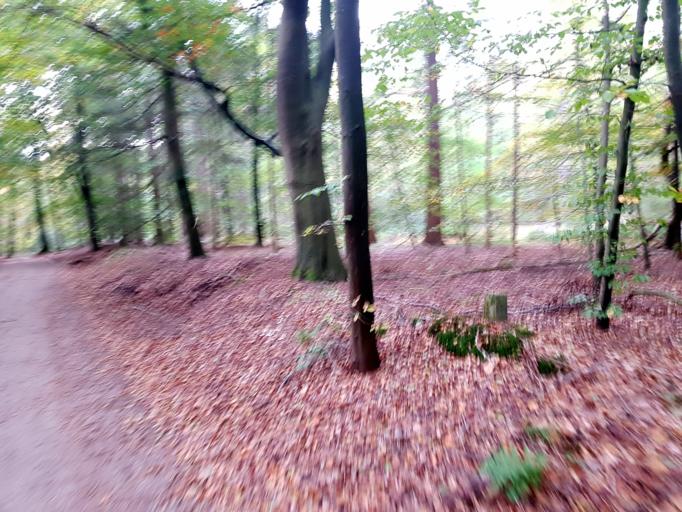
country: NL
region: Utrecht
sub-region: Gemeente Utrechtse Heuvelrug
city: Maarsbergen
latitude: 52.0277
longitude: 5.3986
